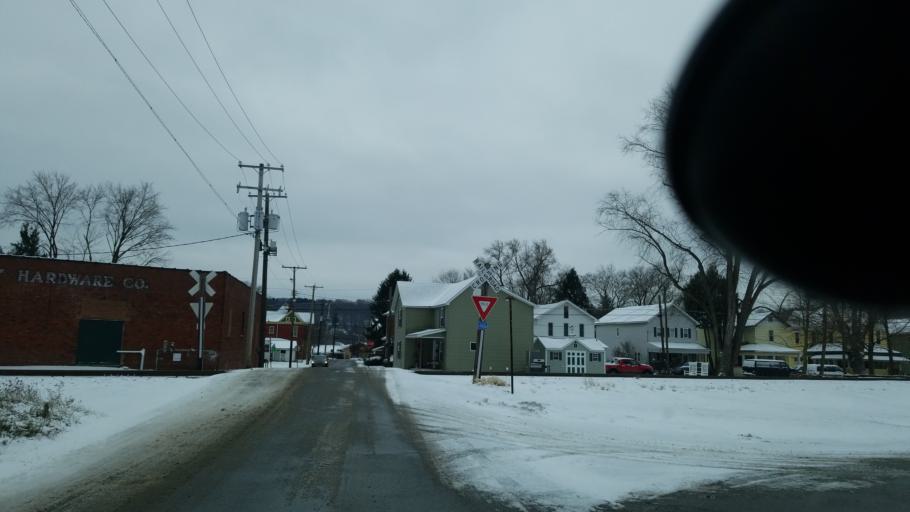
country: US
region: Pennsylvania
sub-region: Jefferson County
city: Punxsutawney
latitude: 40.9444
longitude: -78.9769
